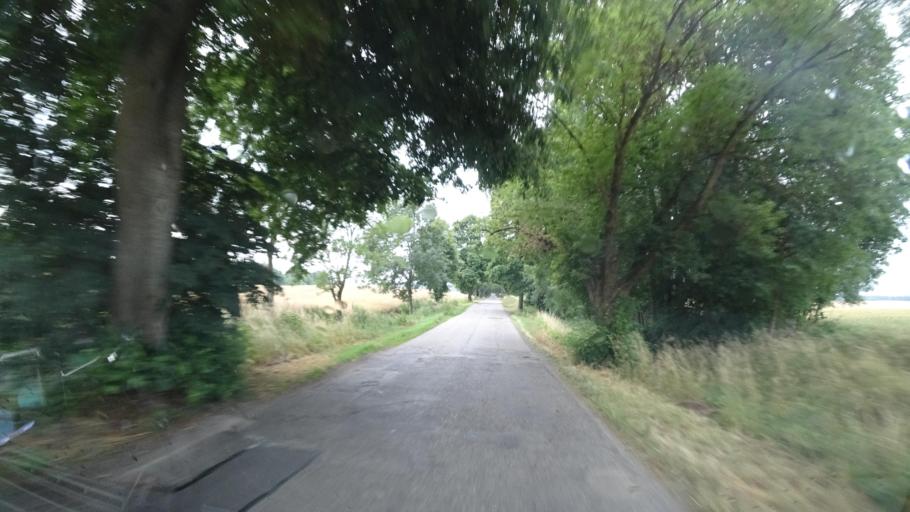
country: PL
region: Warmian-Masurian Voivodeship
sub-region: Powiat gizycki
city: Ryn
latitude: 53.9149
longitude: 21.5575
